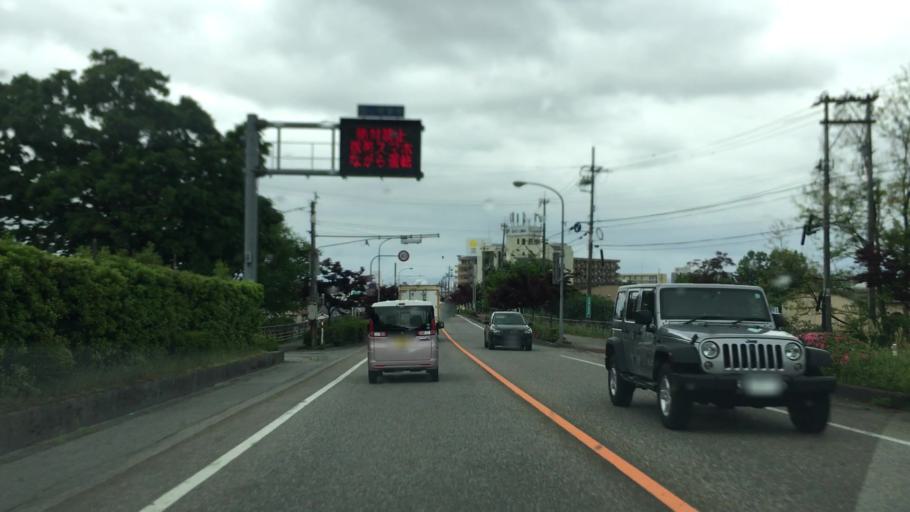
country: JP
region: Toyama
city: Toyama-shi
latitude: 36.7049
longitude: 137.1826
